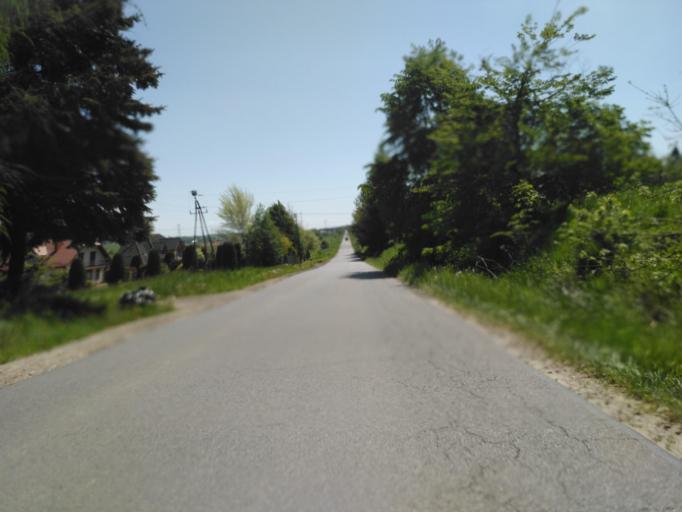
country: PL
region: Subcarpathian Voivodeship
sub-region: Powiat krosnienski
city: Miejsce Piastowe
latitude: 49.6114
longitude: 21.7603
